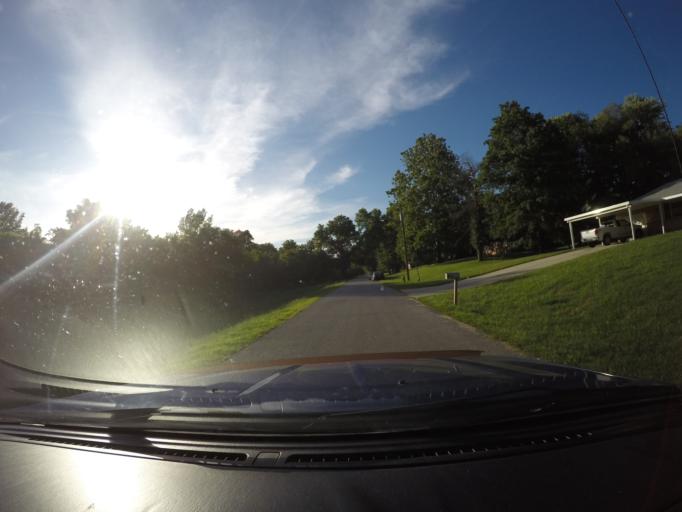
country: US
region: Missouri
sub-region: Platte County
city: Parkville
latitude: 39.1454
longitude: -94.7610
